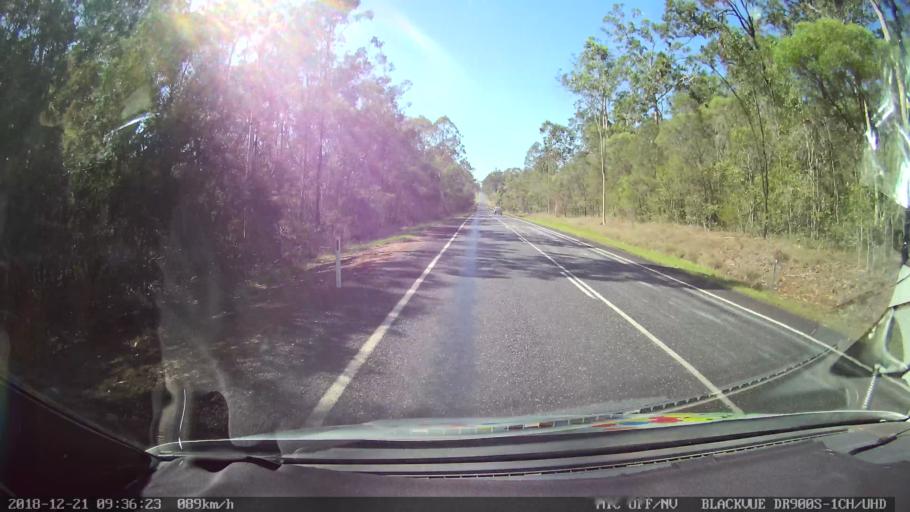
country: AU
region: New South Wales
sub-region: Clarence Valley
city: Grafton
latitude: -29.5225
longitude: 152.9830
